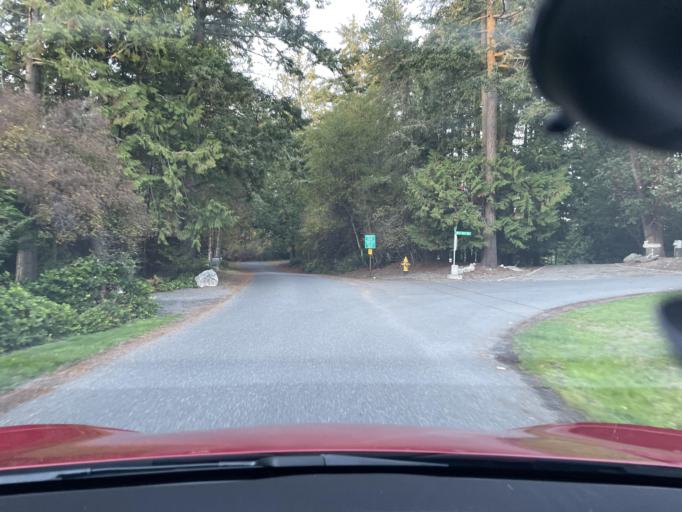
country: US
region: Washington
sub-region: San Juan County
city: Friday Harbor
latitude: 48.6198
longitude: -123.1496
